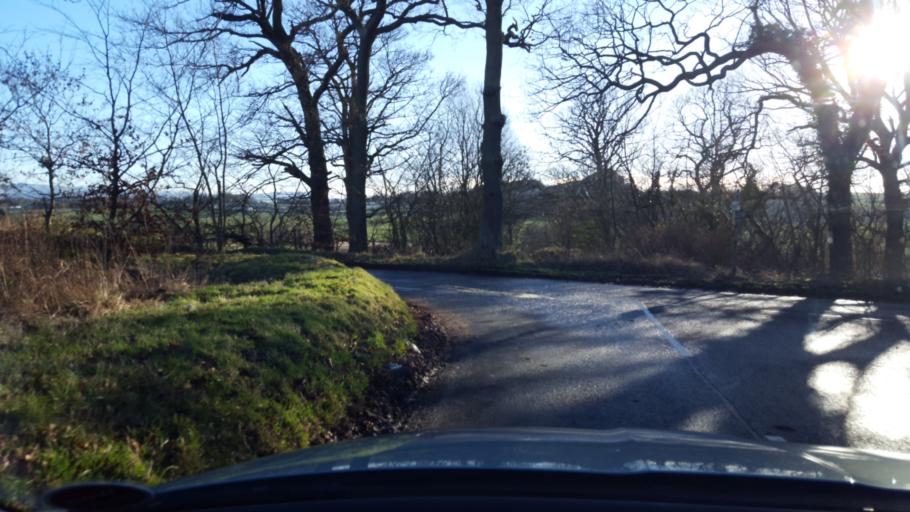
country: GB
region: Scotland
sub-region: West Lothian
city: Livingston
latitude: 55.9550
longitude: -3.5352
